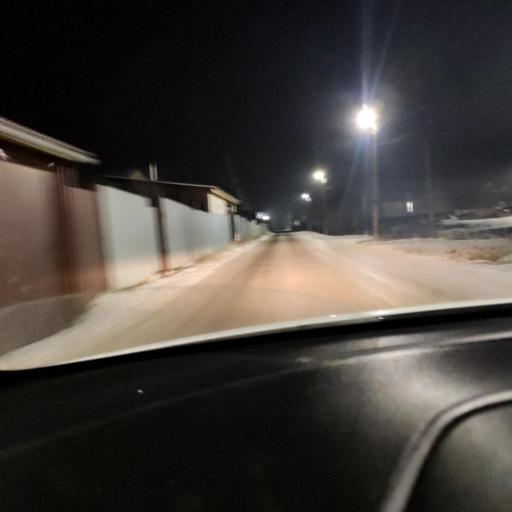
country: RU
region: Tatarstan
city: Staroye Arakchino
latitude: 55.8826
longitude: 49.0403
